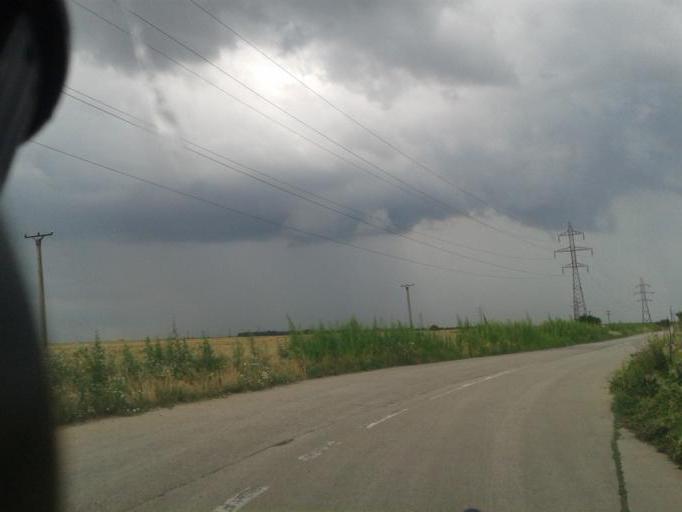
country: RO
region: Calarasi
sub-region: Comuna Belciugatele
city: Belciugatele
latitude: 44.5391
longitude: 26.4606
